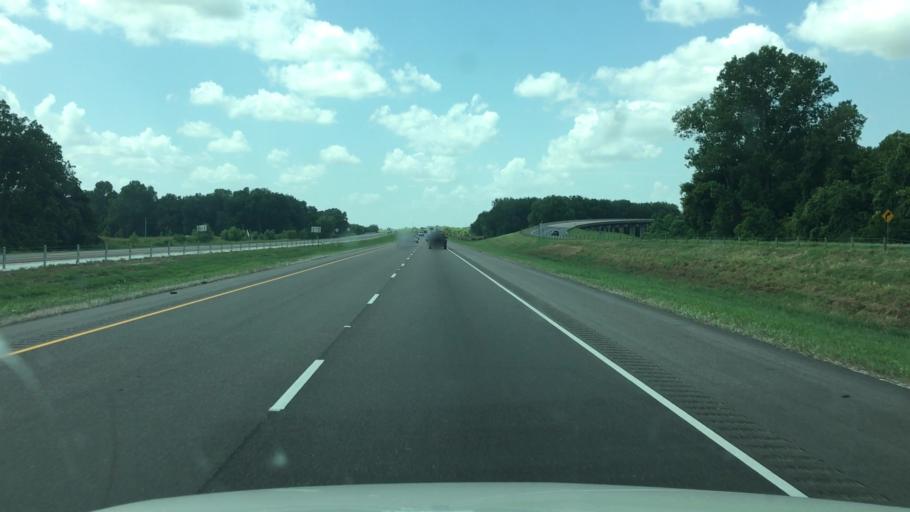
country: US
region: Arkansas
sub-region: Hempstead County
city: Hope
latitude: 33.5928
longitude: -93.8325
